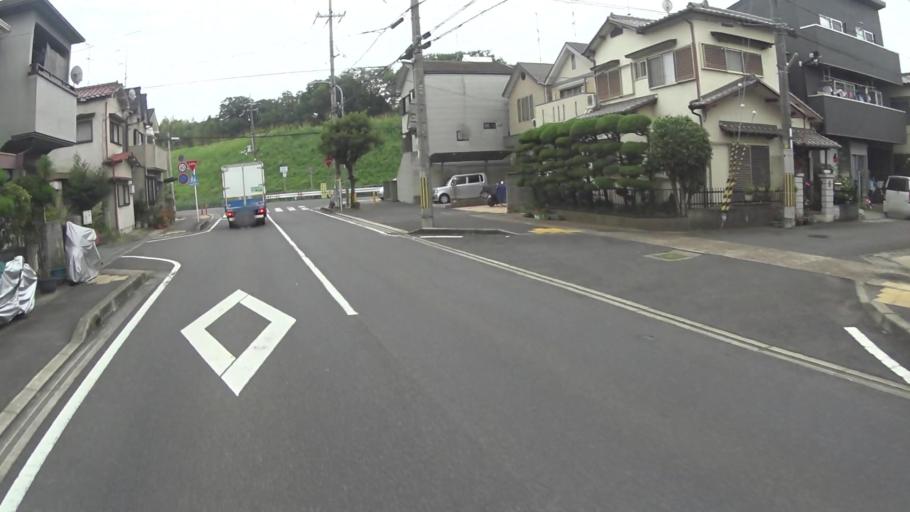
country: JP
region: Kyoto
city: Tanabe
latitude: 34.8368
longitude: 135.7672
